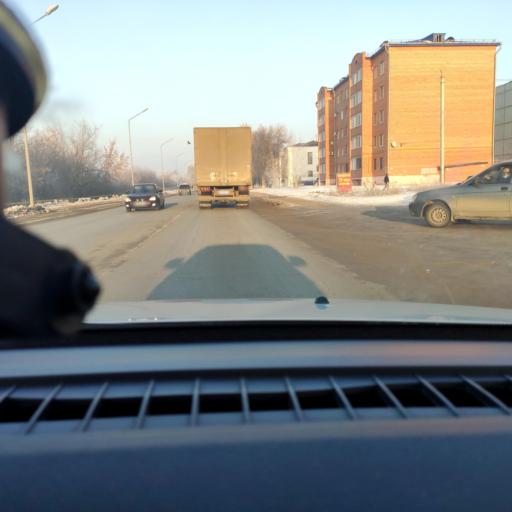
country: RU
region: Samara
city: Chapayevsk
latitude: 52.9704
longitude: 49.6982
